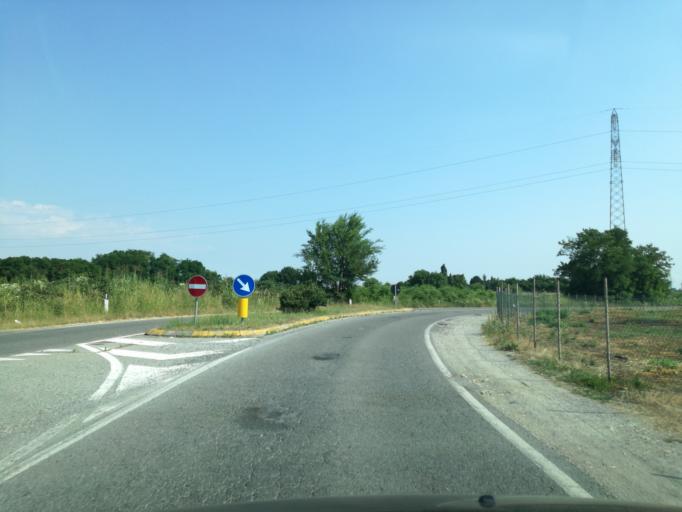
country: IT
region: Lombardy
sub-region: Provincia di Lecco
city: Cernusco Lombardone
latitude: 45.6876
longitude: 9.4026
